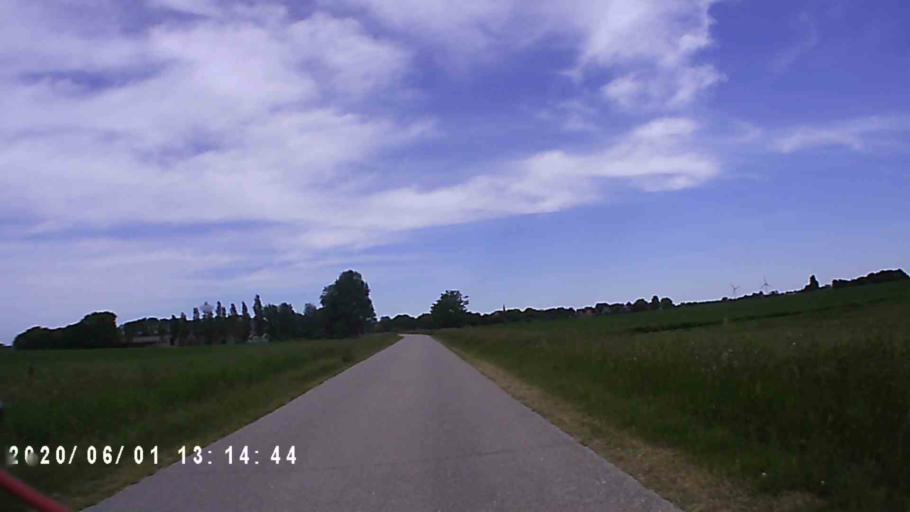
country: NL
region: Friesland
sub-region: Gemeente Littenseradiel
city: Wommels
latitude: 53.1190
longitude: 5.5588
